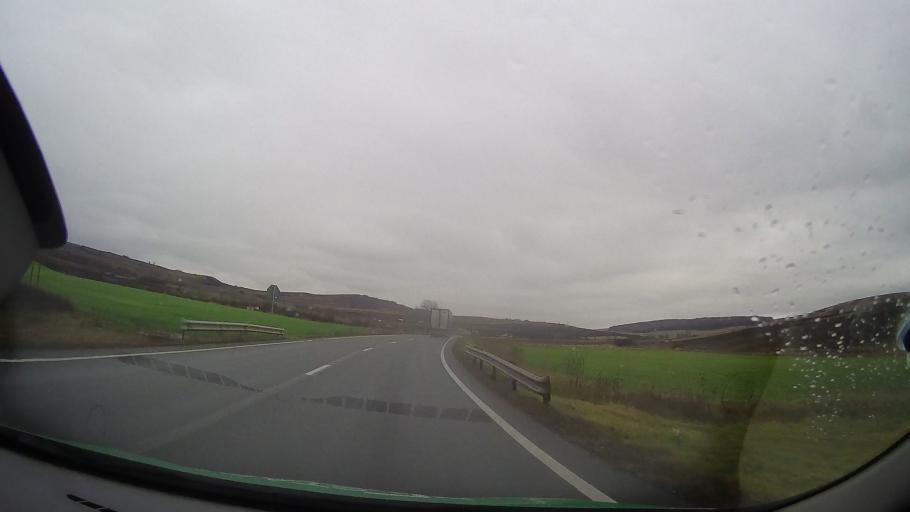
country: RO
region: Mures
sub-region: Comuna Lunca
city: Lunca
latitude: 46.8728
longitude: 24.5491
